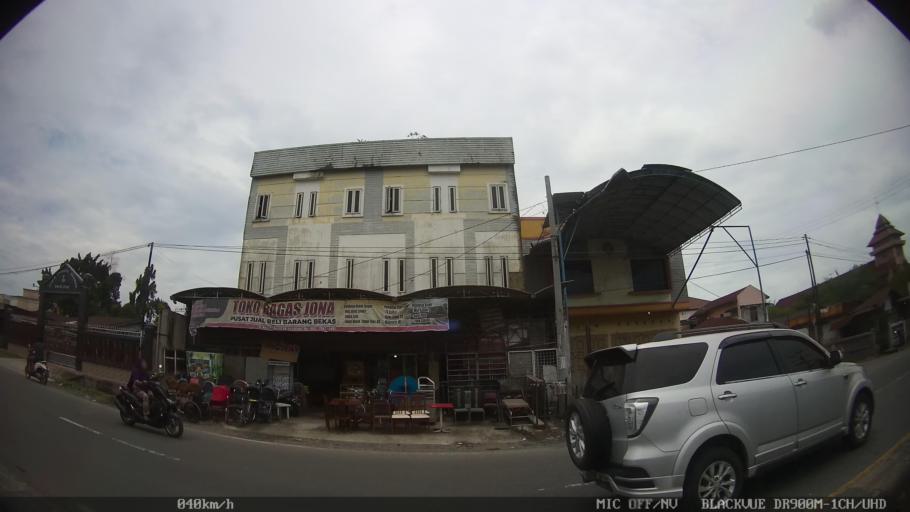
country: ID
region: North Sumatra
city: Sunggal
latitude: 3.5995
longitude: 98.5572
